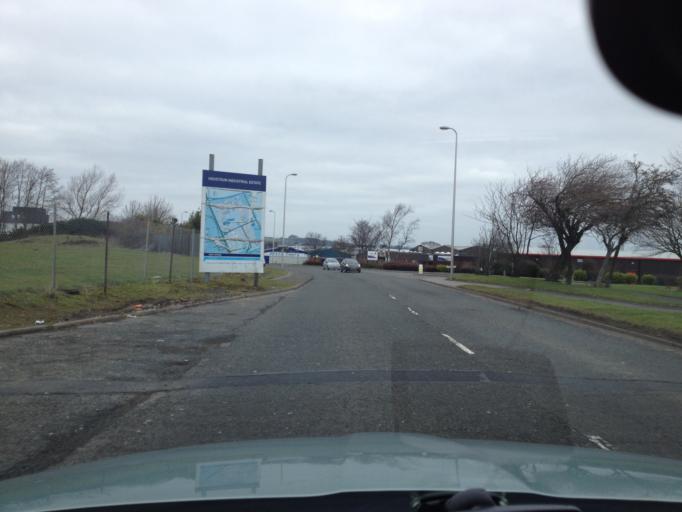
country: GB
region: Scotland
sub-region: West Lothian
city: Livingston
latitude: 55.9045
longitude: -3.5007
